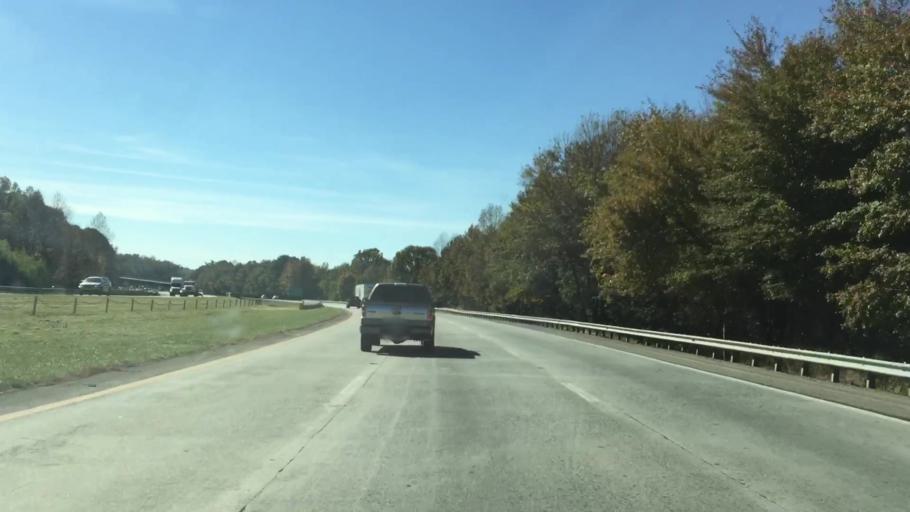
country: US
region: North Carolina
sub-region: Davidson County
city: Thomasville
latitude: 35.8606
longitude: -80.0824
